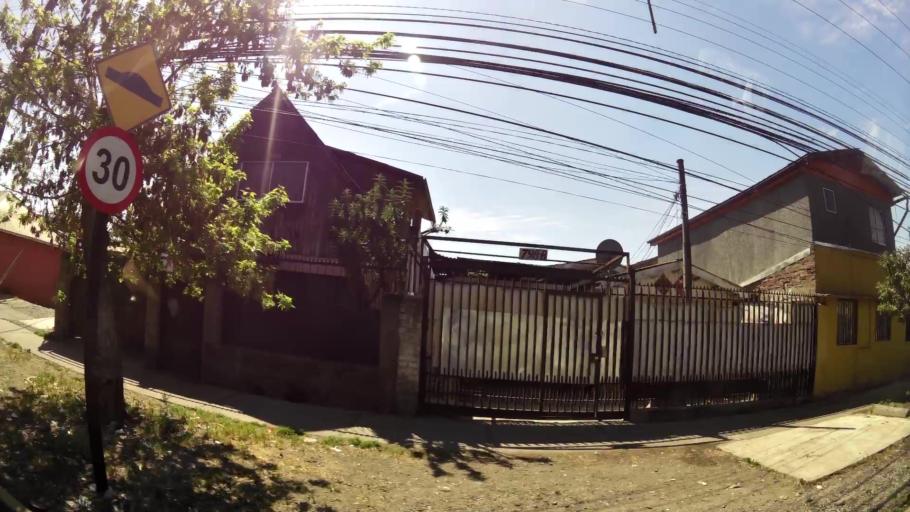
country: CL
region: Santiago Metropolitan
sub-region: Provincia de Santiago
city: La Pintana
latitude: -33.5278
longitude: -70.6533
